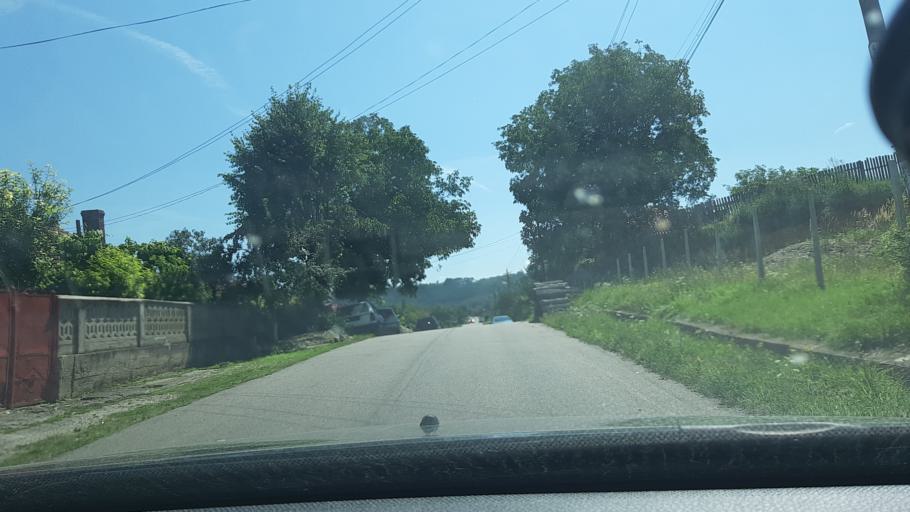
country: RO
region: Hunedoara
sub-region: Comuna Teliucu Inferior
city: Teliucu Inferior
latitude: 45.7009
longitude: 22.8880
